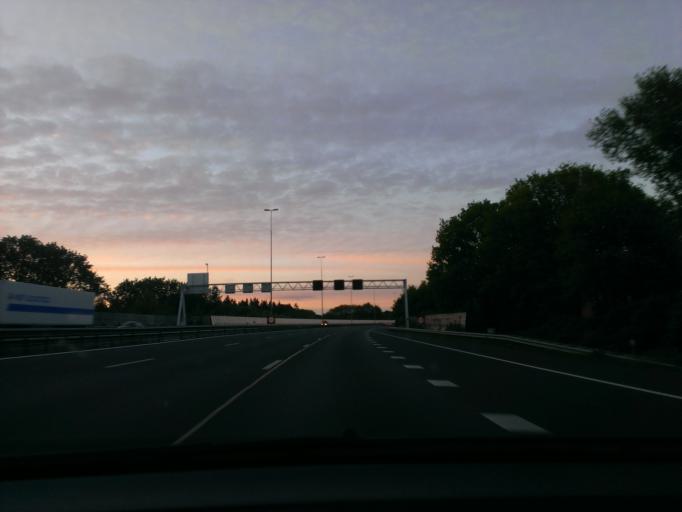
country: NL
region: Gelderland
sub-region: Gemeente Renkum
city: Heelsum
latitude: 51.9789
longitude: 5.7627
